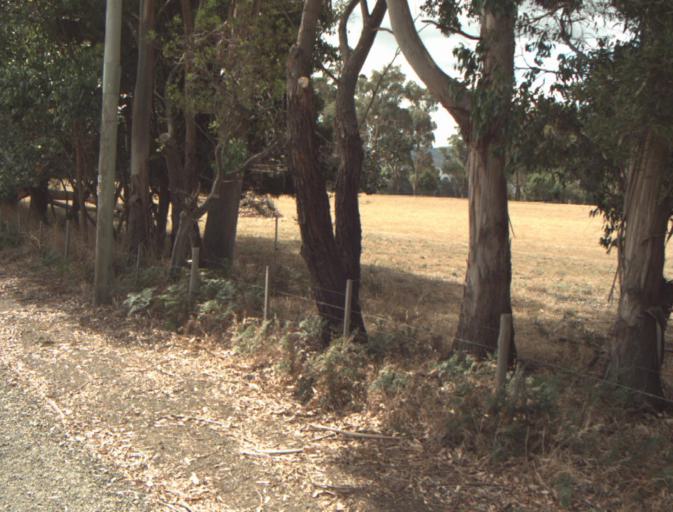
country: AU
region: Tasmania
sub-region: Launceston
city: Mayfield
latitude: -41.2992
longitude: 146.9906
